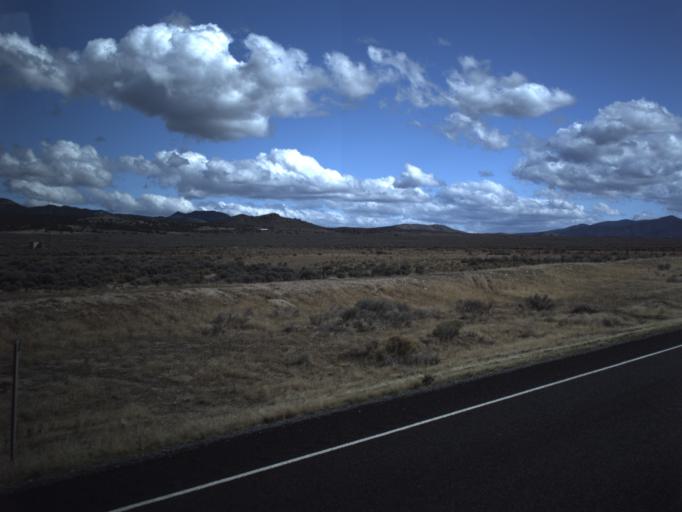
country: US
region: Utah
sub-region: Beaver County
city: Milford
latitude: 38.2797
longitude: -112.9627
